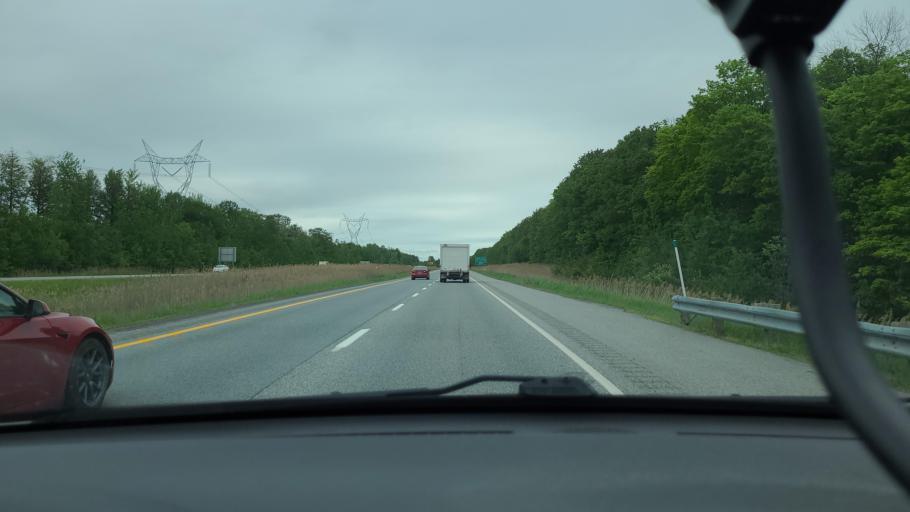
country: CA
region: Quebec
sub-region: Lanaudiere
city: Mascouche
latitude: 45.8022
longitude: -73.5876
